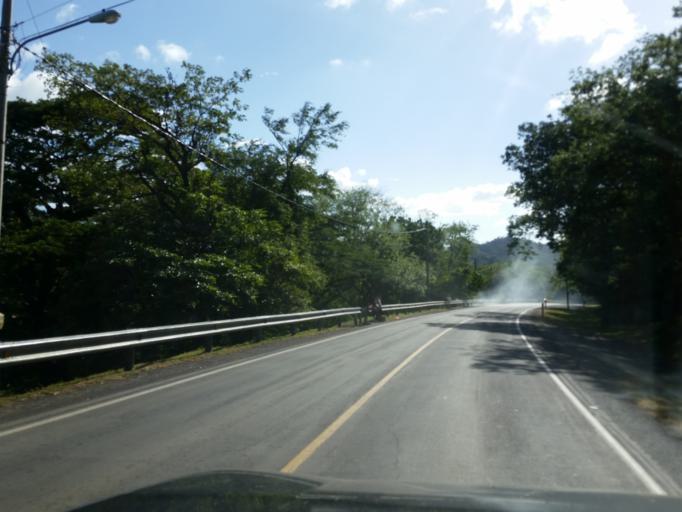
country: NI
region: Rivas
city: San Juan del Sur
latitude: 11.2662
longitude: -85.8481
